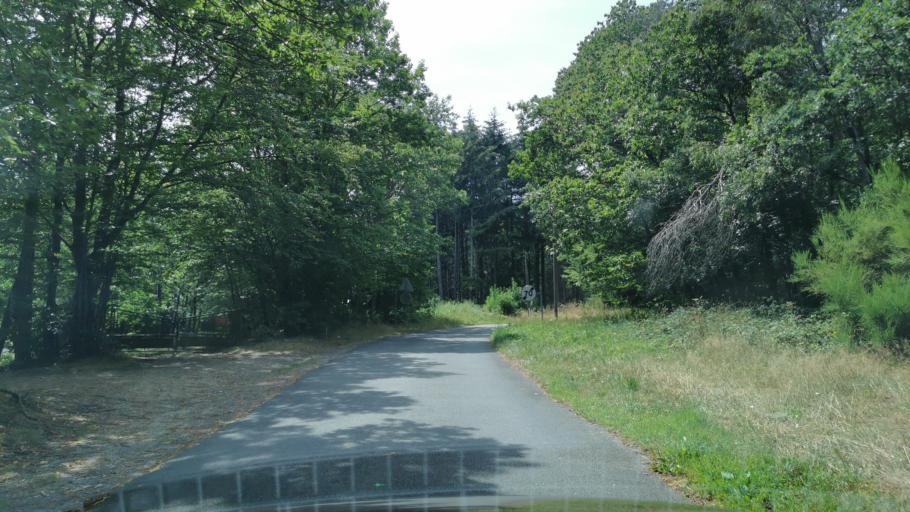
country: FR
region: Bourgogne
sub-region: Departement de Saone-et-Loire
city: Marmagne
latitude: 46.8132
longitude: 4.2772
